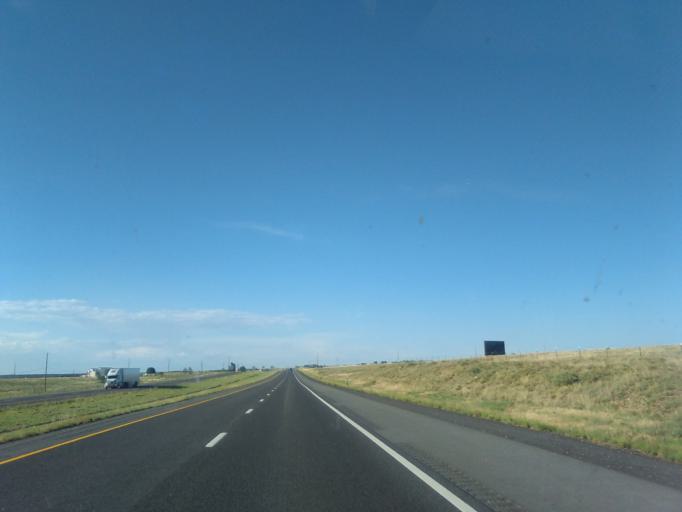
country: US
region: New Mexico
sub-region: San Miguel County
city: Las Vegas
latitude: 35.6337
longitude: -105.2001
